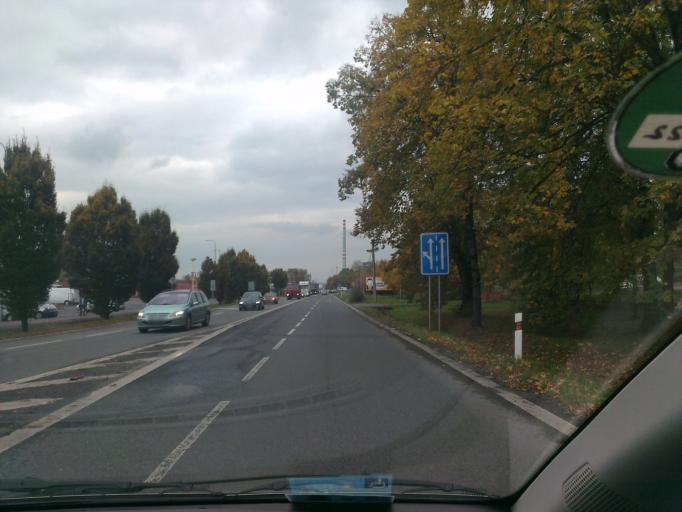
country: CZ
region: Zlin
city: Valasske Mezirici
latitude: 49.4854
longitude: 17.9643
